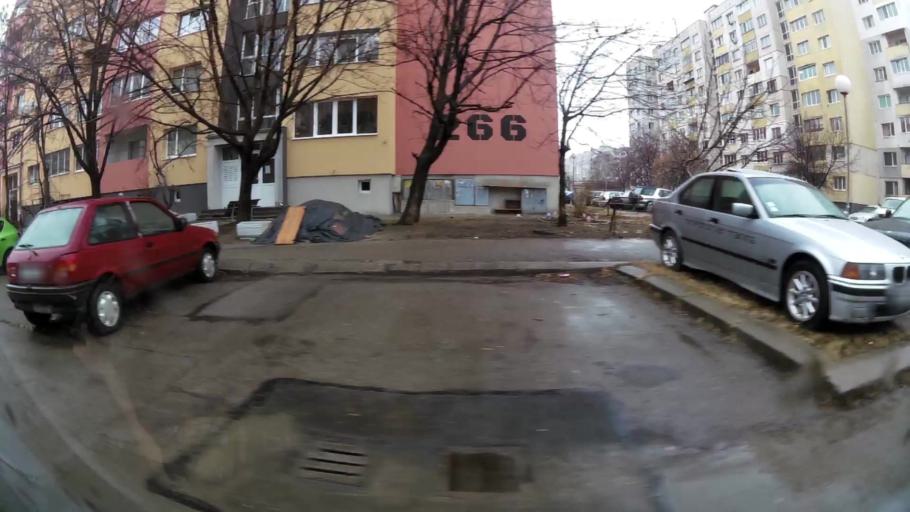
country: BG
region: Sofia-Capital
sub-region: Stolichna Obshtina
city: Sofia
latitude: 42.6496
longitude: 23.4022
